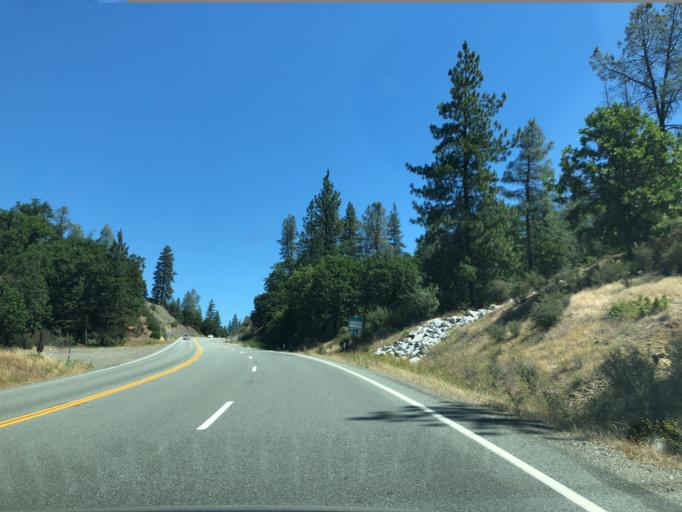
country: US
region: California
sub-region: Trinity County
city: Weaverville
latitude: 40.6691
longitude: -122.8847
